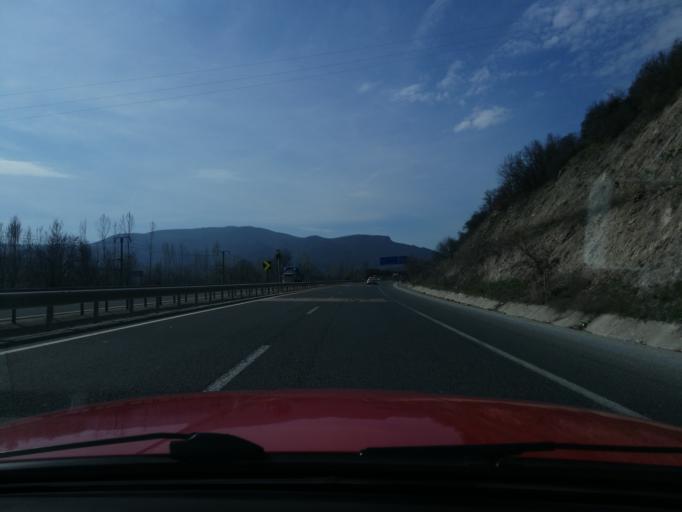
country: TR
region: Bilecik
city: Bozuyuk
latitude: 39.9906
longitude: 30.0046
